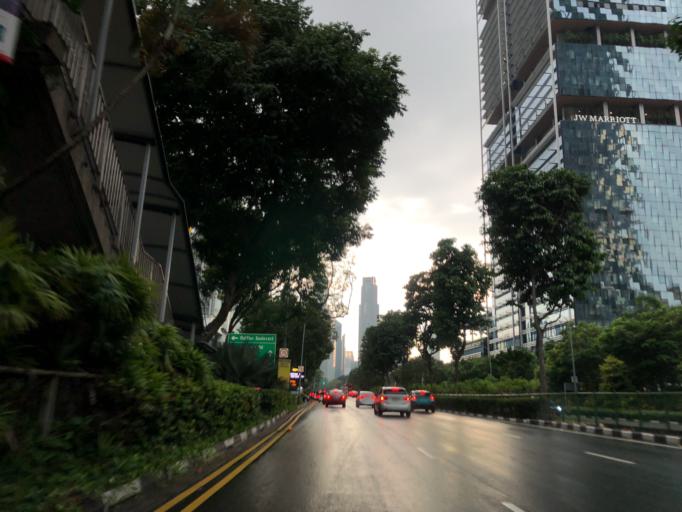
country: SG
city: Singapore
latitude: 1.2951
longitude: 103.8571
